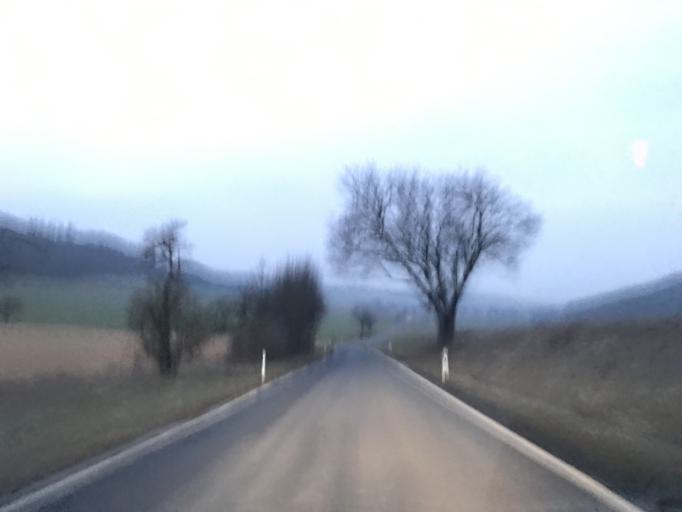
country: DE
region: Hesse
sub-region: Regierungsbezirk Kassel
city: Hofgeismar
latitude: 51.5123
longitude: 9.3884
